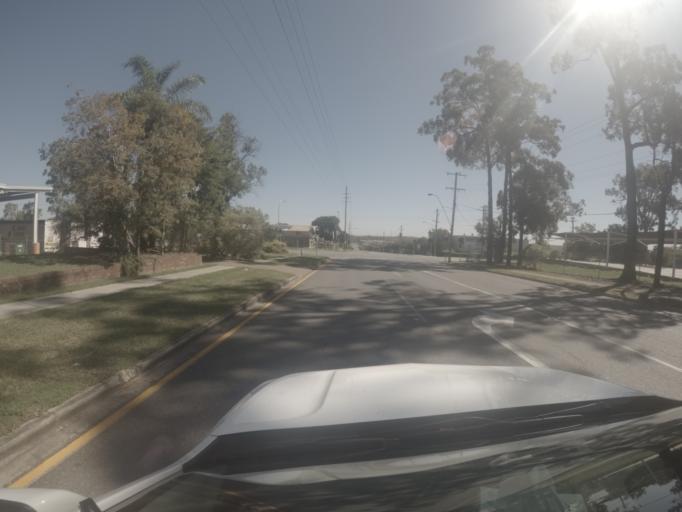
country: AU
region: Queensland
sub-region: Brisbane
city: Richlands
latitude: -27.5781
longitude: 152.9562
